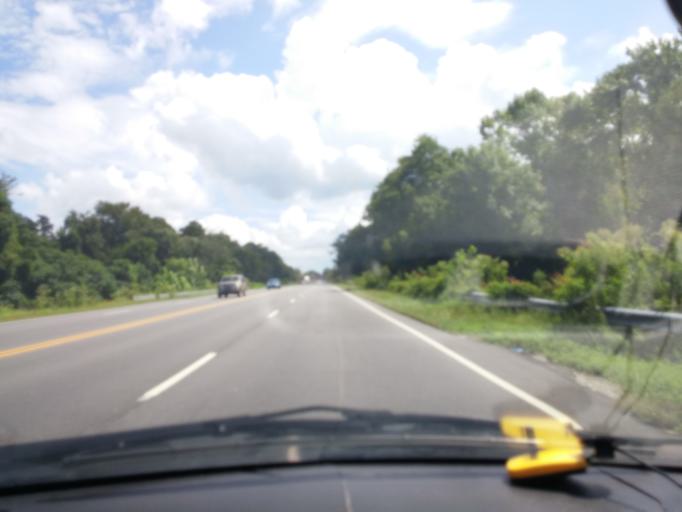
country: US
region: North Carolina
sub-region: Lenoir County
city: Kinston
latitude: 35.2589
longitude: -77.5886
